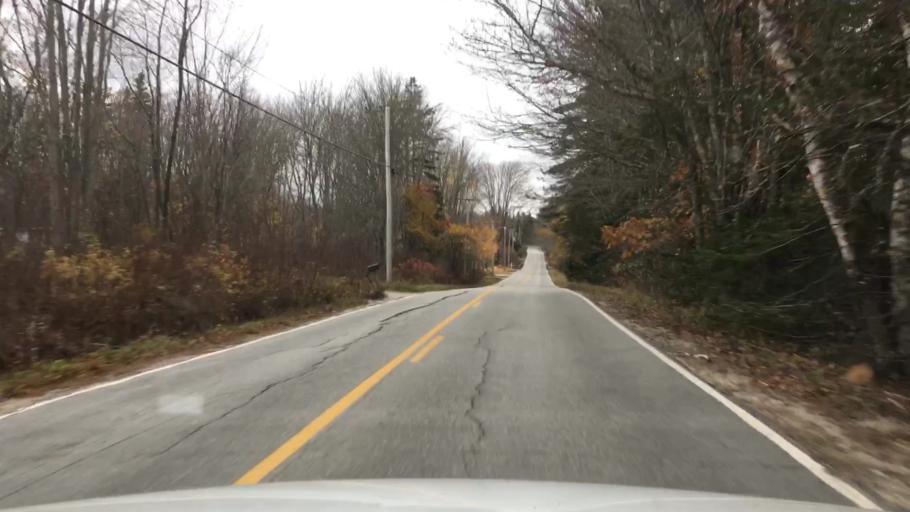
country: US
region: Maine
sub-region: Hancock County
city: Sedgwick
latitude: 44.2730
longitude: -68.5645
